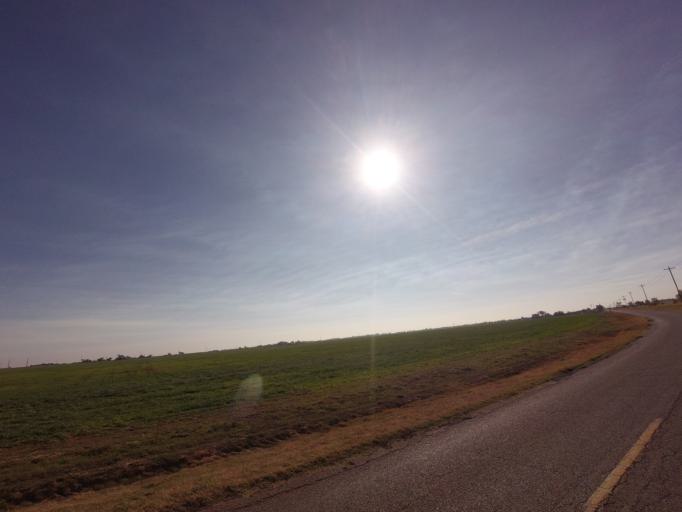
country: US
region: New Mexico
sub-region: Curry County
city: Clovis
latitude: 34.4113
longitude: -103.1611
